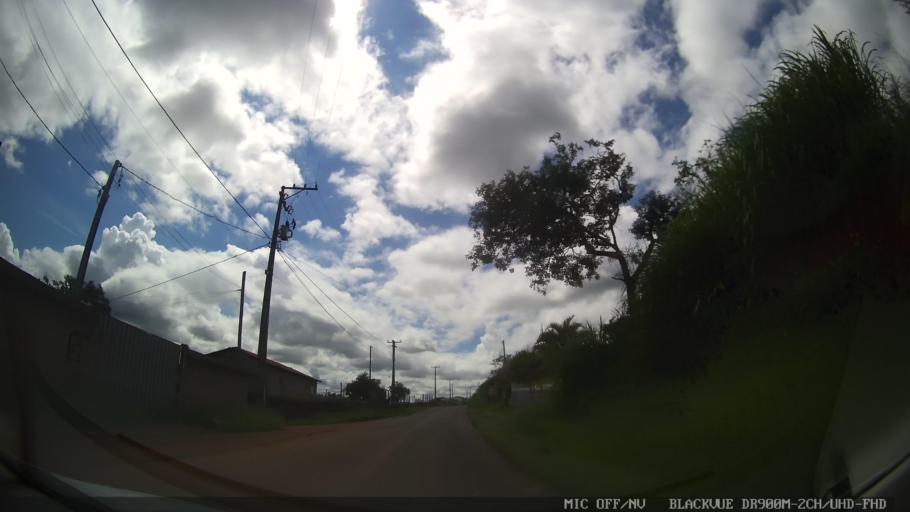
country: BR
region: Sao Paulo
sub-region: Amparo
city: Amparo
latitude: -22.8592
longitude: -46.7122
